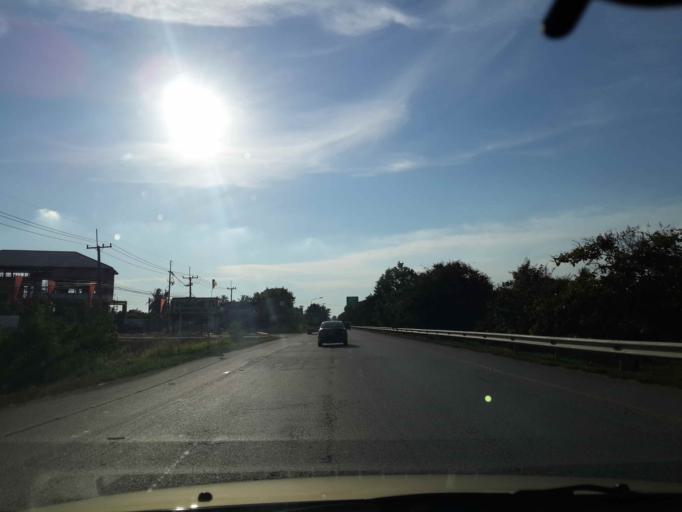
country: TH
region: Chon Buri
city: Bang Lamung
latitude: 12.9732
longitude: 100.9683
